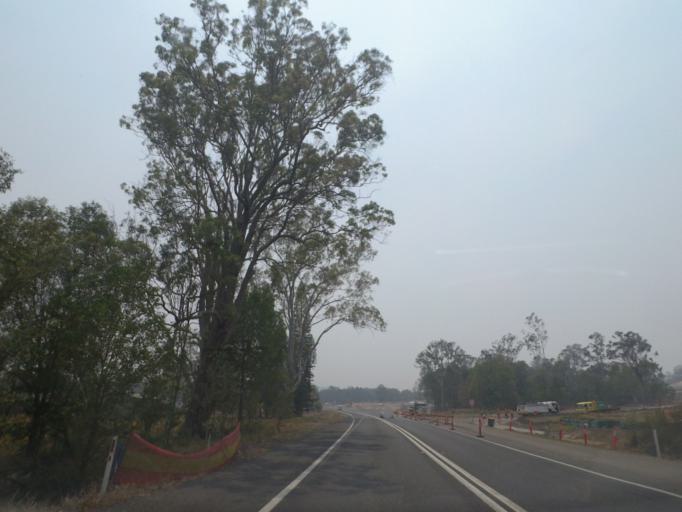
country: AU
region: New South Wales
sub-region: Clarence Valley
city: Maclean
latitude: -29.5521
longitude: 153.1541
